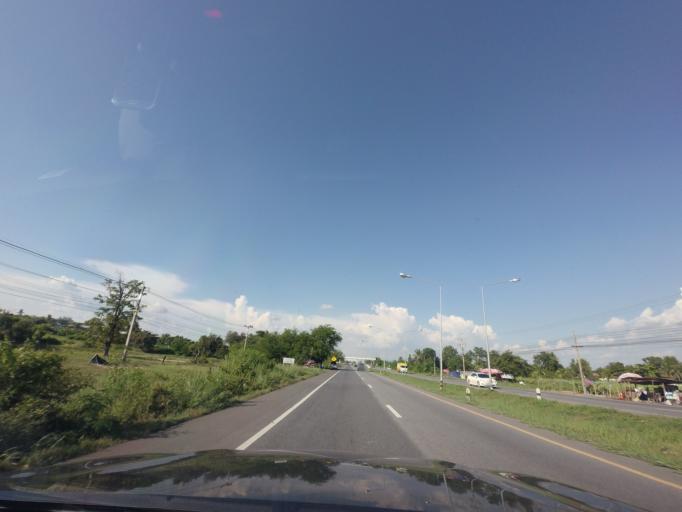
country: TH
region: Khon Kaen
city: Non Sila
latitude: 15.9490
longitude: 102.6820
